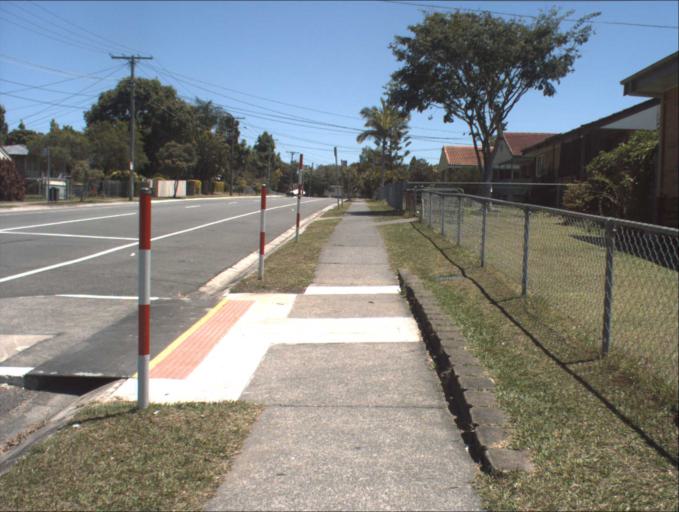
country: AU
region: Queensland
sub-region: Logan
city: Logan City
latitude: -27.6360
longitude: 153.1105
